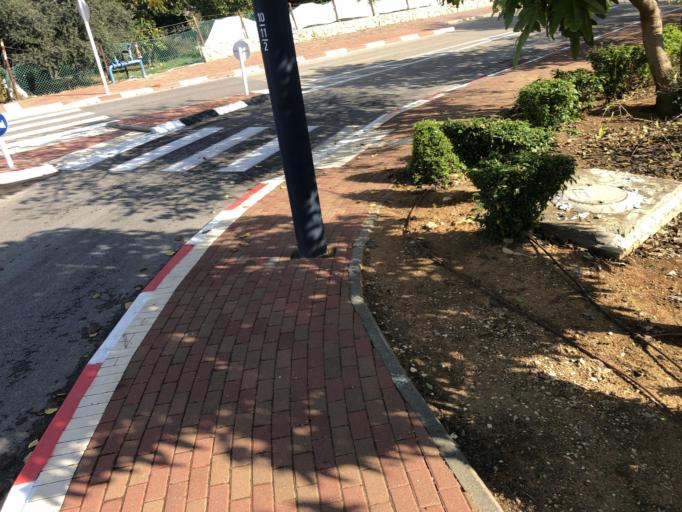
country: IL
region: Northern District
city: `Akko
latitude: 32.9399
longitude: 35.0929
